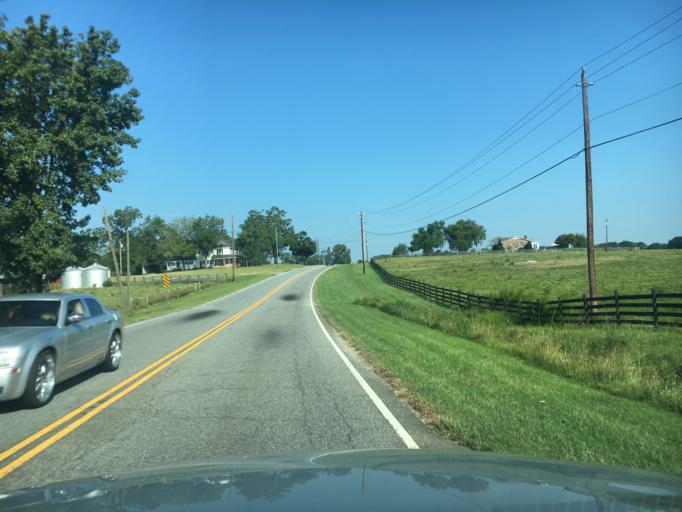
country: US
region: South Carolina
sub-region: Anderson County
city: Honea Path
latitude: 34.4552
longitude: -82.4094
